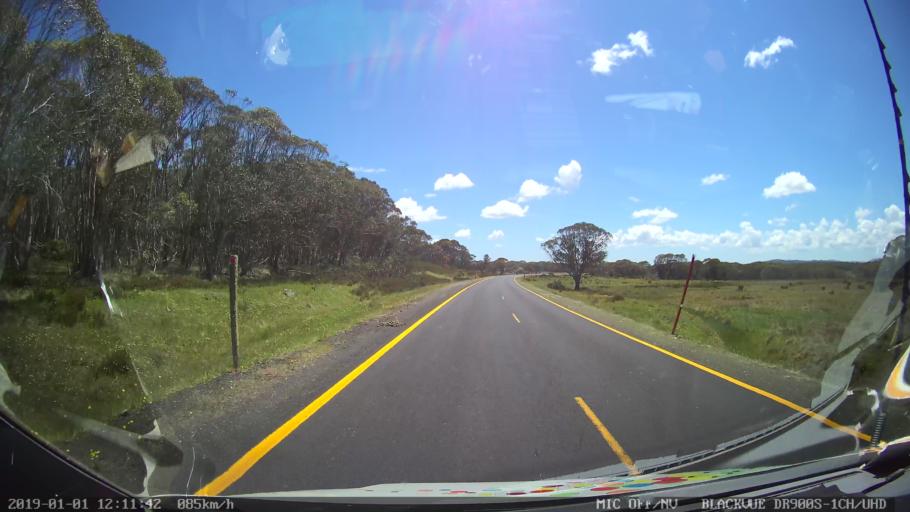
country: AU
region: New South Wales
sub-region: Tumut Shire
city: Tumut
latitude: -35.7809
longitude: 148.5088
